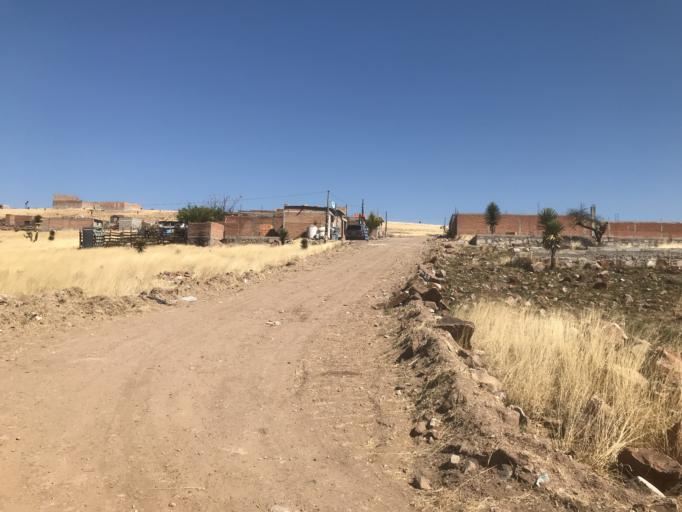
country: MX
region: Durango
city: Victoria de Durango
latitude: 24.0351
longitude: -104.7140
